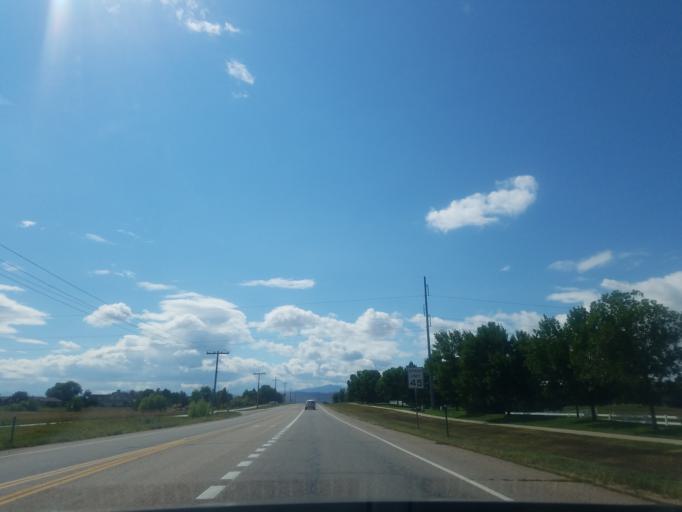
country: US
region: Colorado
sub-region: Larimer County
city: Loveland
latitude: 40.4801
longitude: -105.0478
